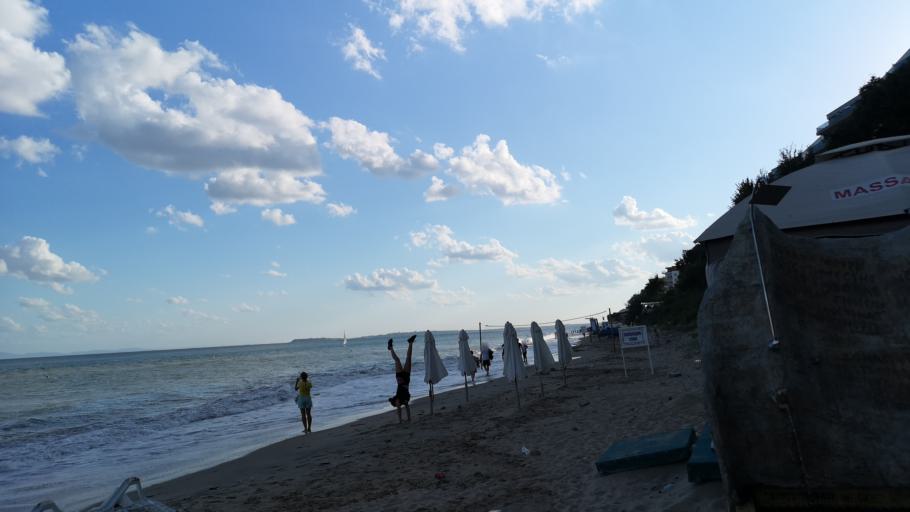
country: BG
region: Burgas
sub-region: Obshtina Nesebur
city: Sveti Vlas
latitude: 42.7039
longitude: 27.7996
